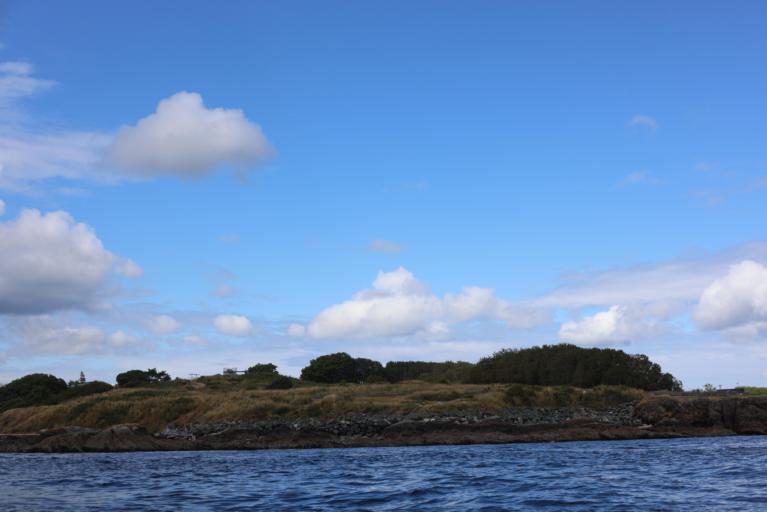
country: CA
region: British Columbia
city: Victoria
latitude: 48.4159
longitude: -123.4109
